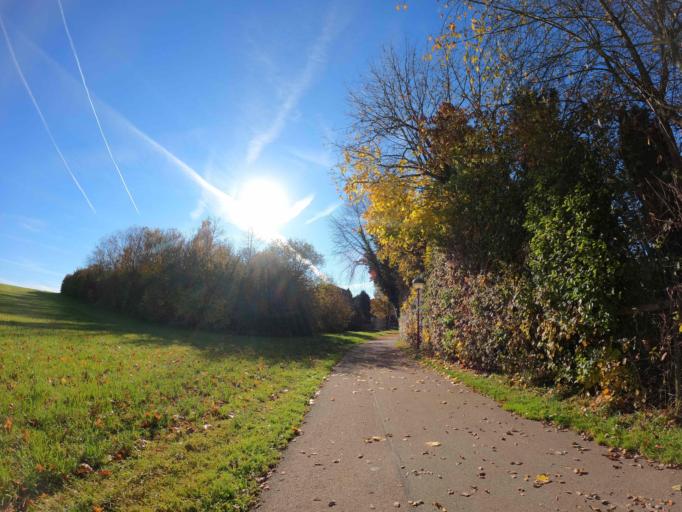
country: DE
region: Bavaria
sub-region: Upper Bavaria
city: Oberhaching
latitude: 48.0257
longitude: 11.6020
